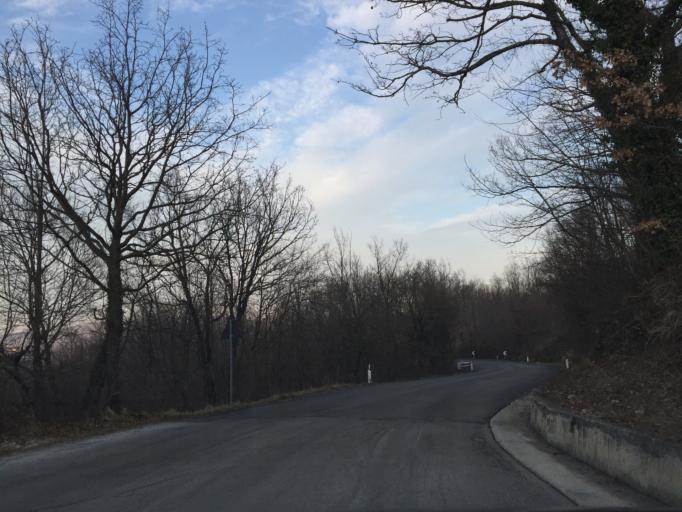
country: IT
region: Molise
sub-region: Provincia di Campobasso
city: Guardiaregia
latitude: 41.4465
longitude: 14.5509
